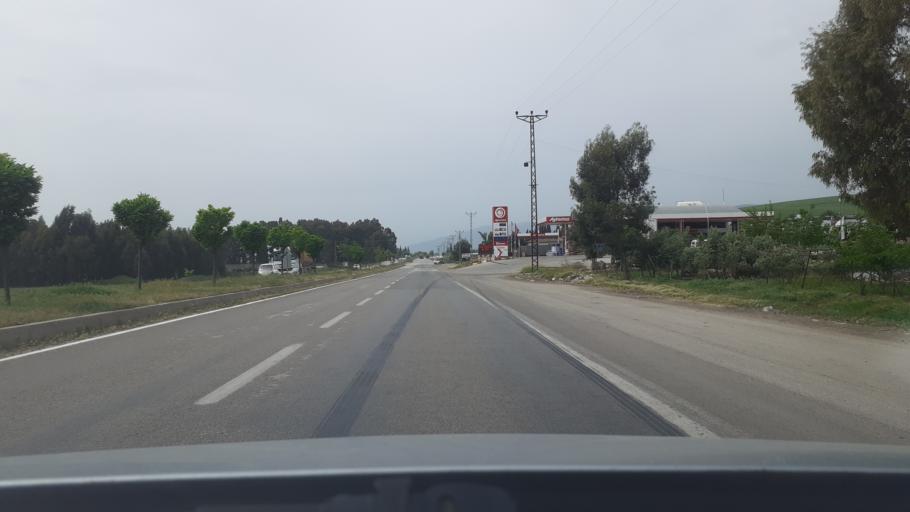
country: TR
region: Hatay
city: Kirikhan
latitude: 36.4678
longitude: 36.3404
